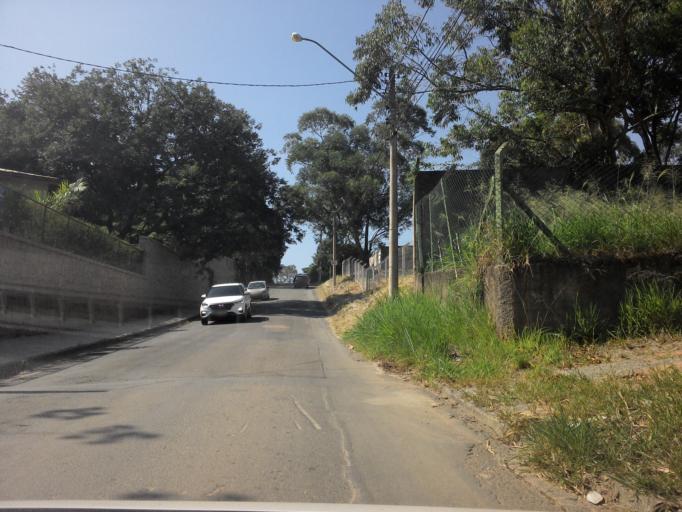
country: BR
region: Sao Paulo
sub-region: Vinhedo
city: Vinhedo
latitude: -23.0112
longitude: -47.0048
